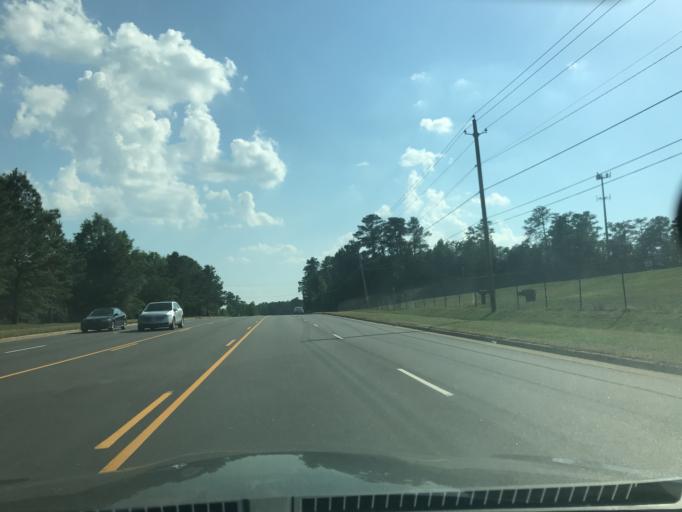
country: US
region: North Carolina
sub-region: Wake County
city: Wake Forest
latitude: 35.9118
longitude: -78.5970
